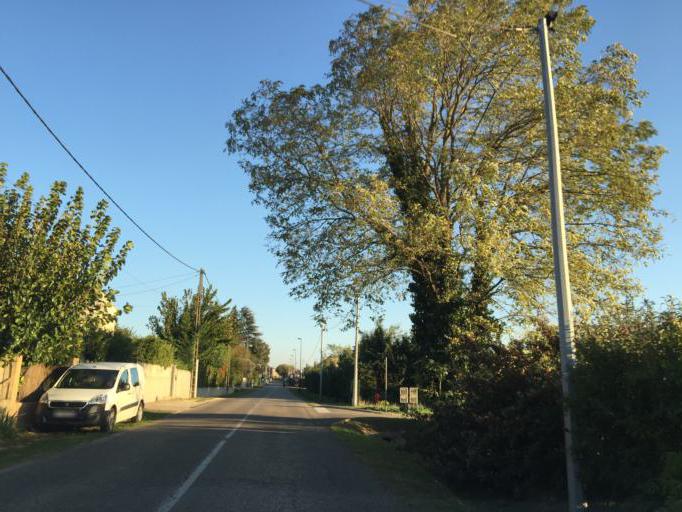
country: FR
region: Rhone-Alpes
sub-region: Departement de la Drome
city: Donzere
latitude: 44.4470
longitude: 4.7031
